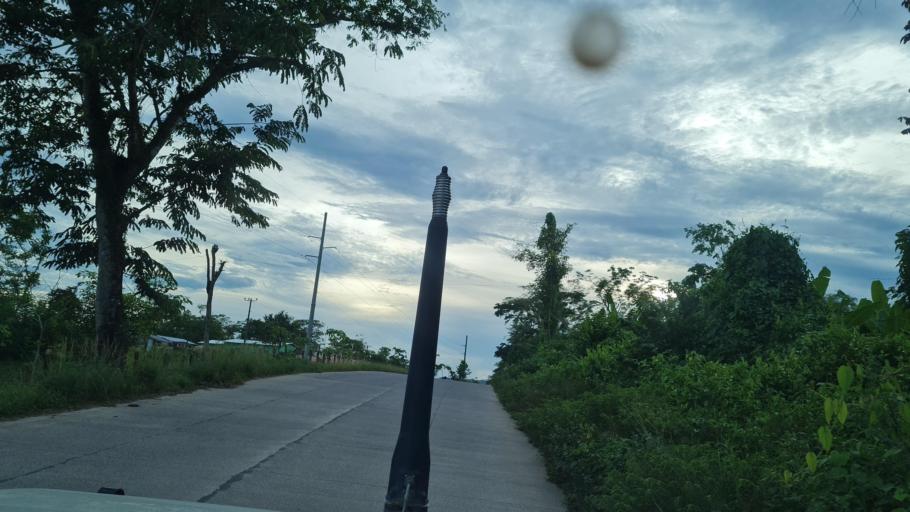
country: NI
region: Atlantico Norte (RAAN)
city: Siuna
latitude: 13.6841
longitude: -84.5945
